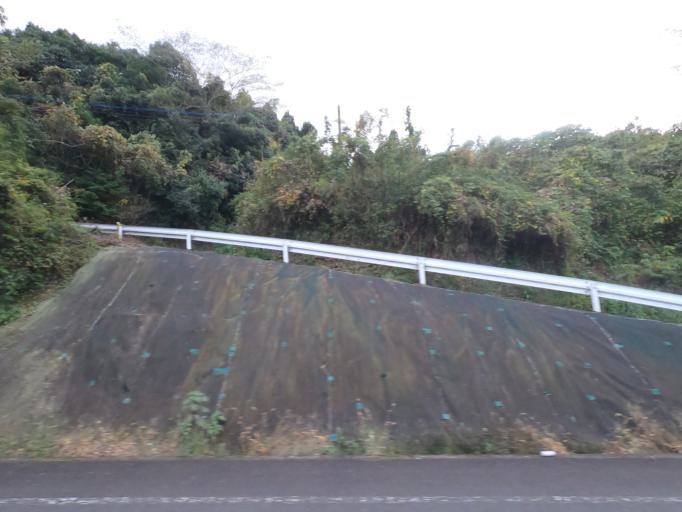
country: JP
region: Kumamoto
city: Minamata
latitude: 32.2626
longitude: 130.5080
